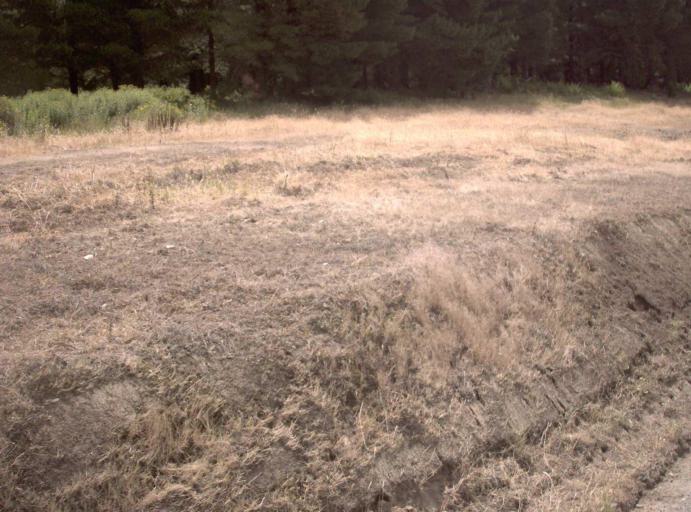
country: AU
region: Victoria
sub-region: Latrobe
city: Traralgon
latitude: -38.3883
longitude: 146.6614
